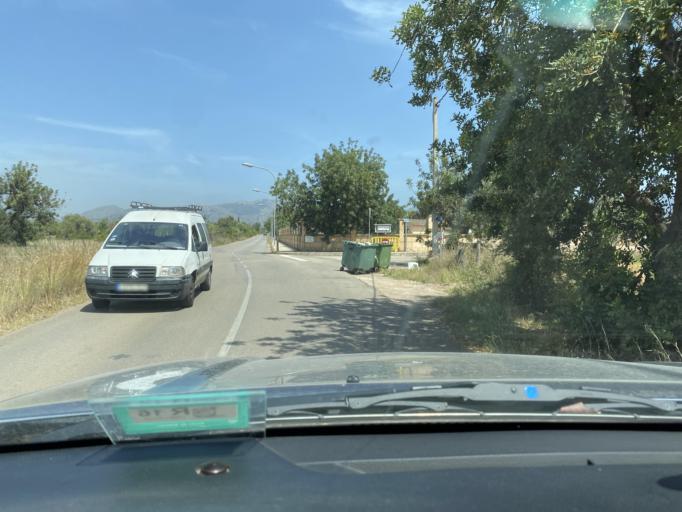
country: ES
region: Balearic Islands
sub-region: Illes Balears
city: Marratxi
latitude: 39.6298
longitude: 2.7106
